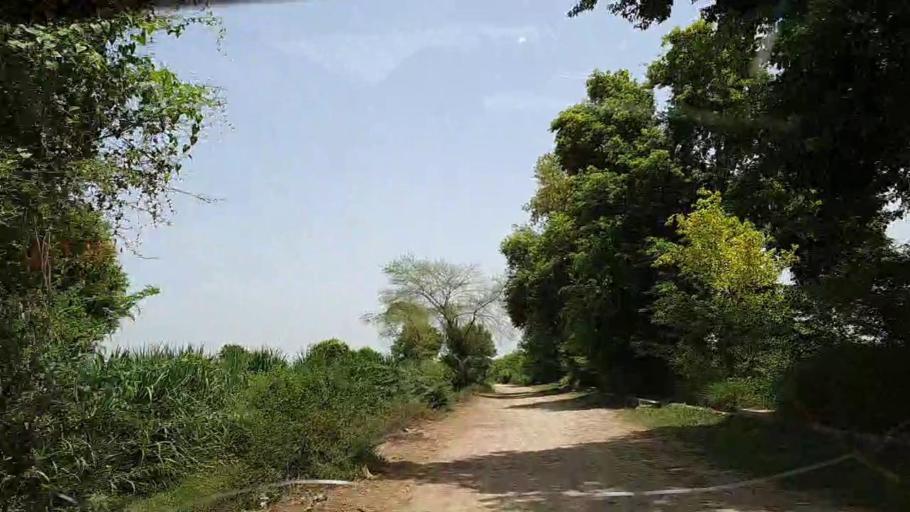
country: PK
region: Sindh
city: Tharu Shah
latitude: 26.9346
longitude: 68.0349
